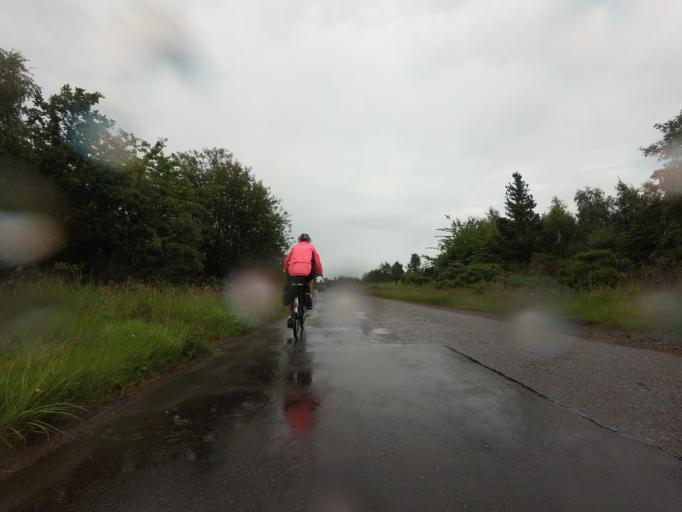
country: GB
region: Scotland
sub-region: Moray
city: Fochabers
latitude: 57.6597
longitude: -3.0676
